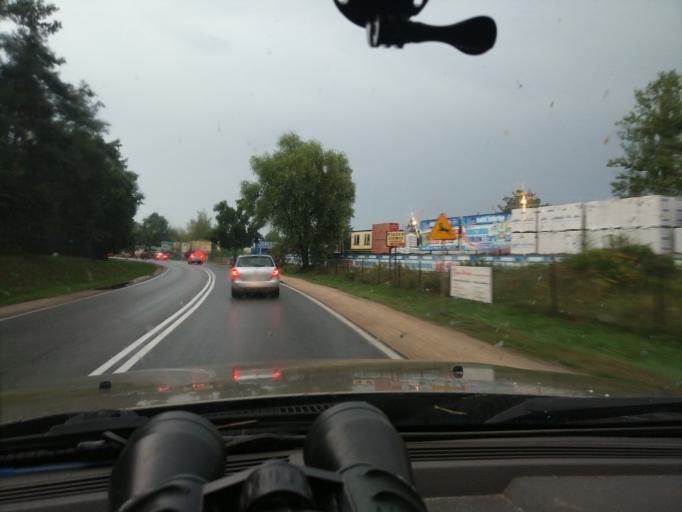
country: PL
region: Masovian Voivodeship
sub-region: Powiat pruszkowski
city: Granica
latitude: 52.1472
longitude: 20.7894
